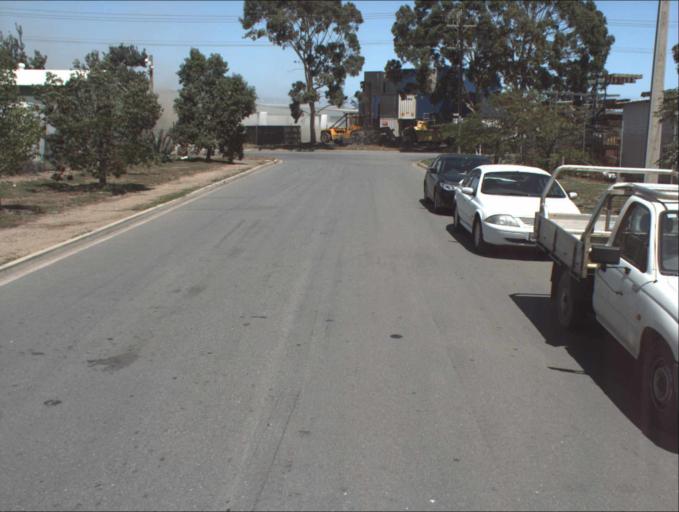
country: AU
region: South Australia
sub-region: Port Adelaide Enfield
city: Alberton
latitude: -34.8379
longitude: 138.5332
